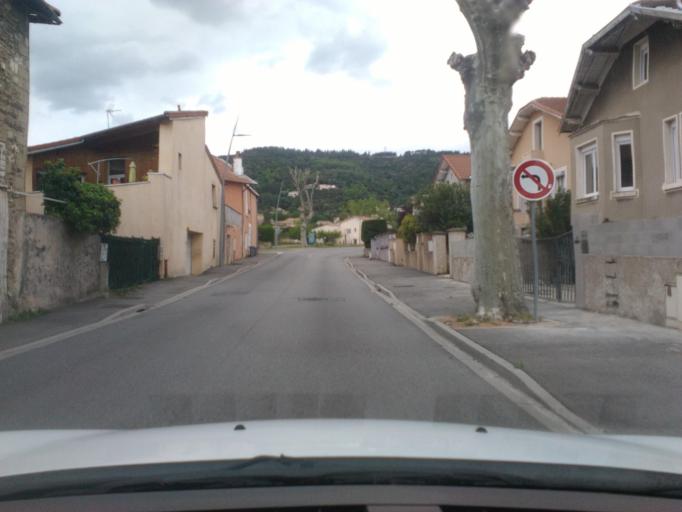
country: FR
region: Rhone-Alpes
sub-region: Departement de l'Ardeche
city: Saint-Peray
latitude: 44.9478
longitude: 4.8443
